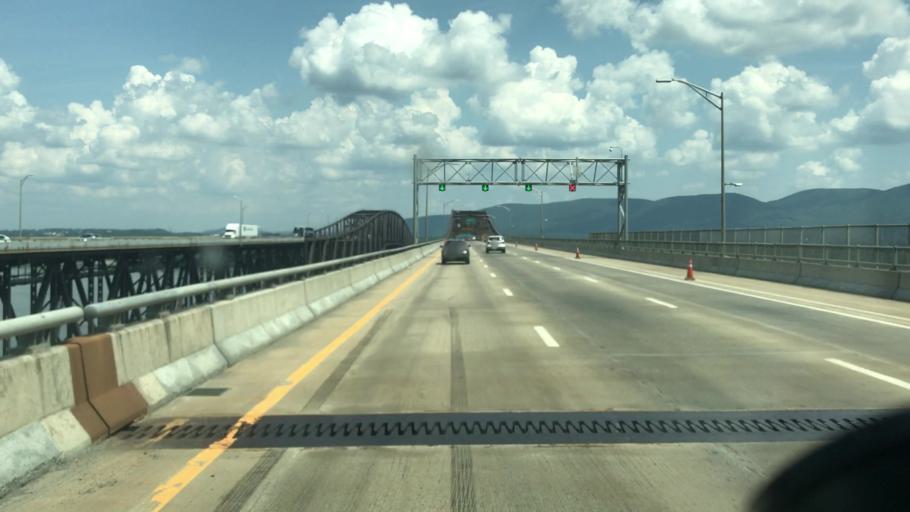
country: US
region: New York
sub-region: Orange County
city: Balmville
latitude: 41.5205
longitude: -74.0068
